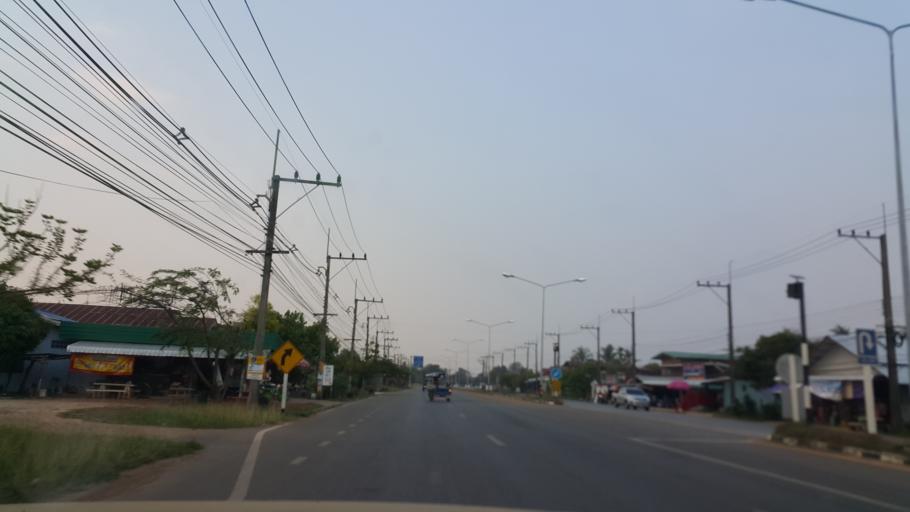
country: TH
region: Nakhon Phanom
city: Renu Nakhon
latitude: 17.0116
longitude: 104.7238
